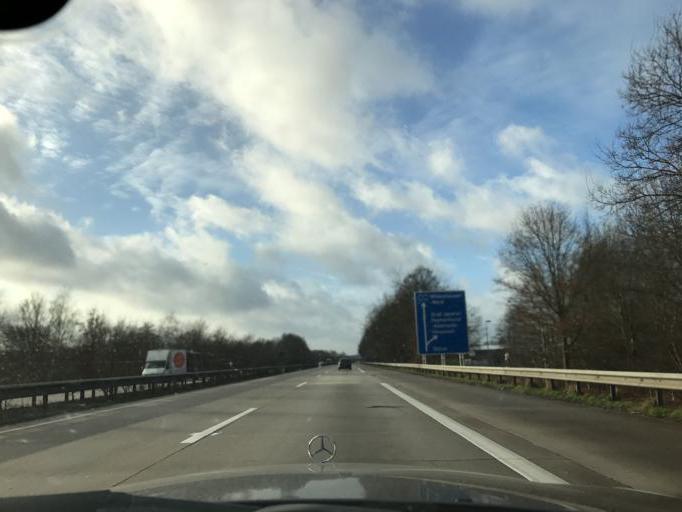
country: DE
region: Lower Saxony
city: Gross Ippener
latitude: 52.9779
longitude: 8.6268
